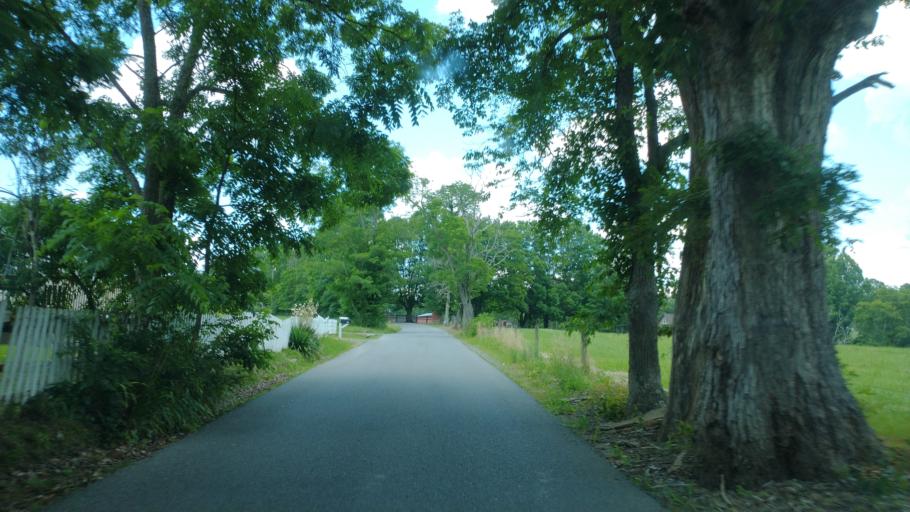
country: US
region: West Virginia
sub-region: Mercer County
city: Athens
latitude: 37.4559
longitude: -81.0291
